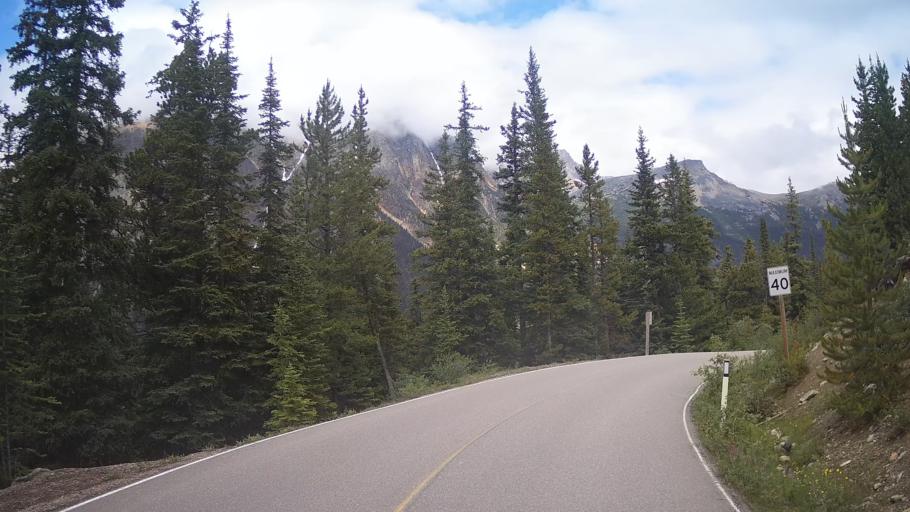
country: CA
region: Alberta
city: Jasper Park Lodge
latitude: 52.7032
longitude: -118.0604
